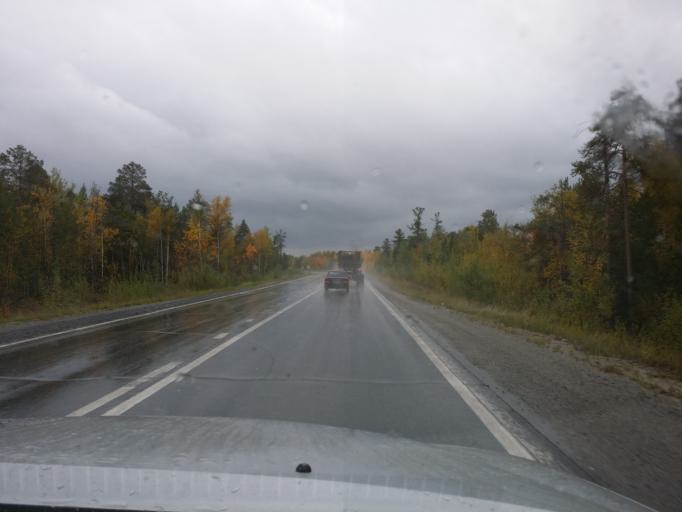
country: RU
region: Khanty-Mansiyskiy Avtonomnyy Okrug
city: Megion
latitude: 61.1354
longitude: 75.7659
